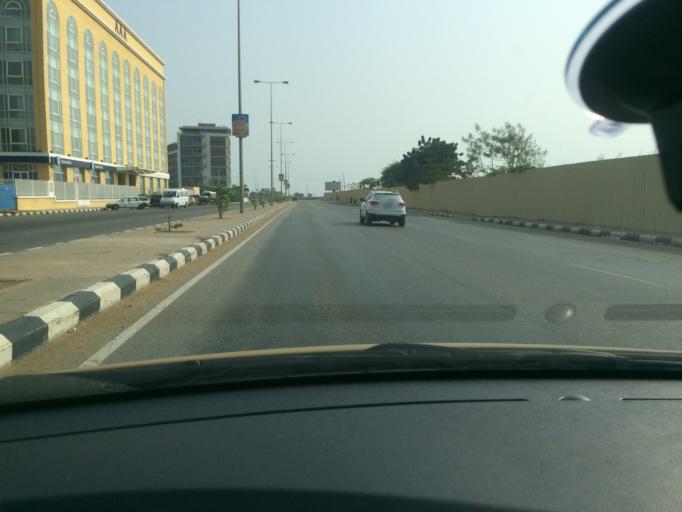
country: AO
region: Luanda
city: Luanda
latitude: -8.8155
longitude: 13.2198
